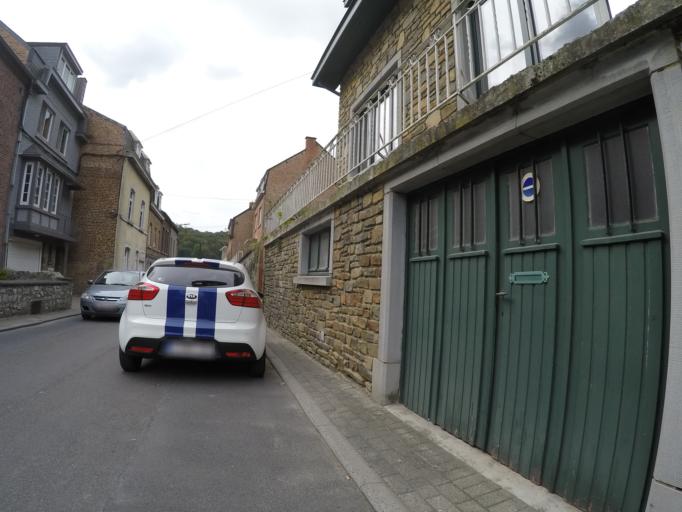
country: BE
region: Wallonia
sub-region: Province de Namur
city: Dinant
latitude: 50.2693
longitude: 4.9090
